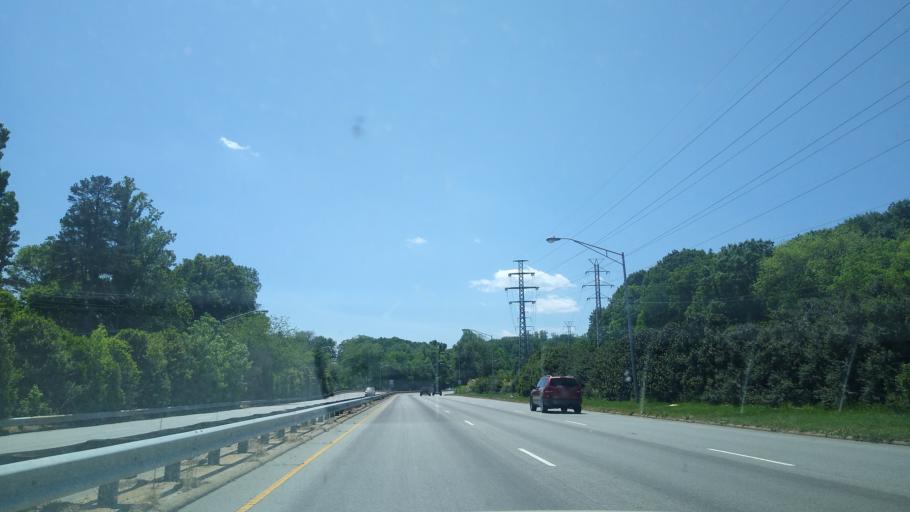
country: US
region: North Carolina
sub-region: Guilford County
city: Greensboro
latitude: 36.0716
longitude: -79.8370
